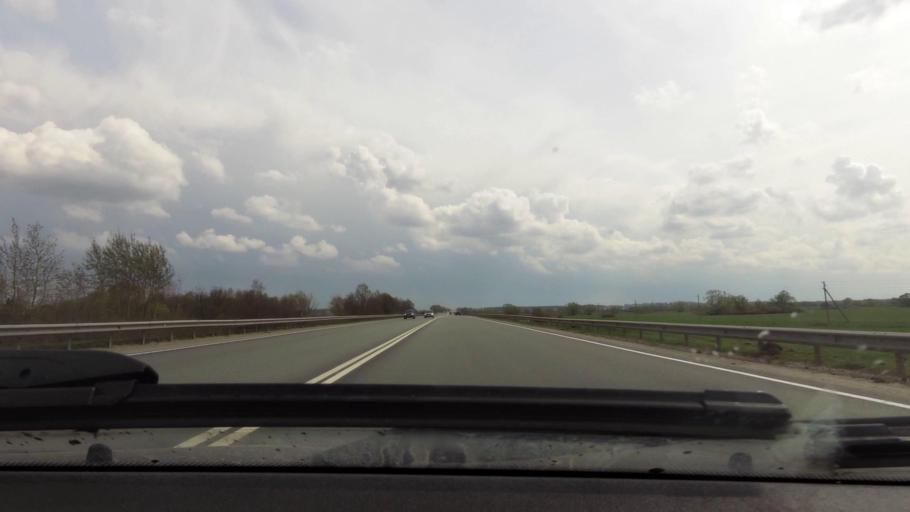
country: RU
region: Rjazan
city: Bagramovo
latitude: 54.7470
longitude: 39.4316
